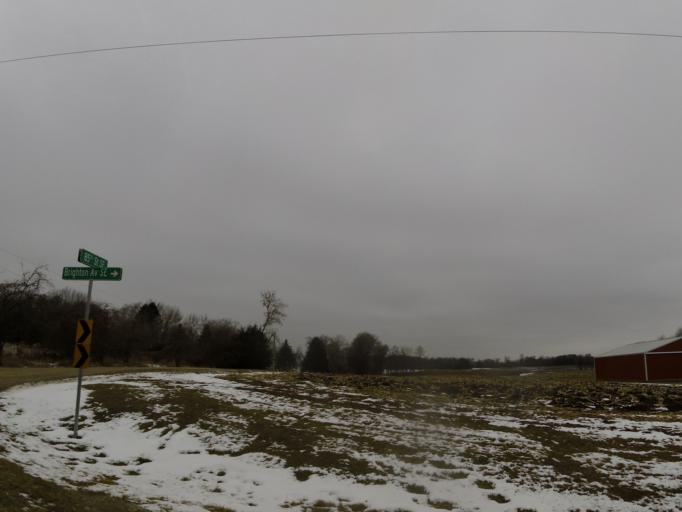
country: US
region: Minnesota
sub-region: Wright County
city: Montrose
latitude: 45.0287
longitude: -93.8584
